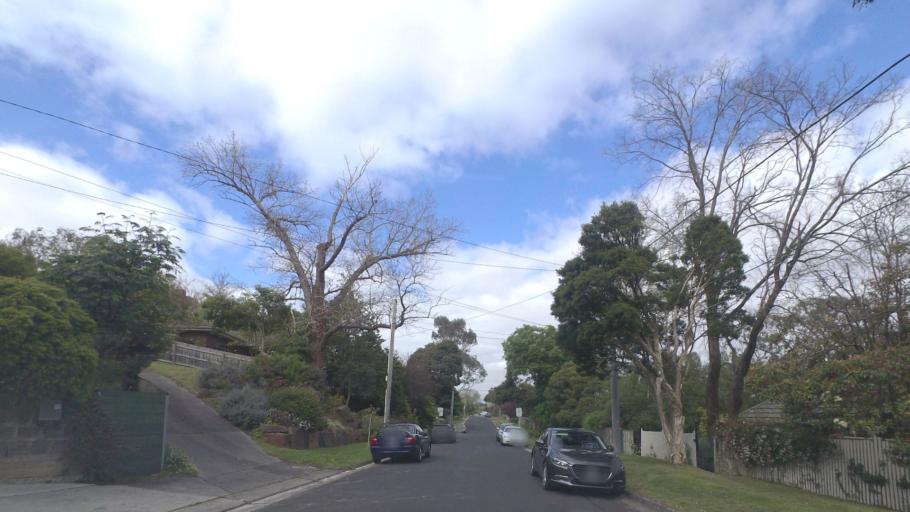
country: AU
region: Victoria
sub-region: Maroondah
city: Croydon South
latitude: -37.8040
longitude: 145.2591
